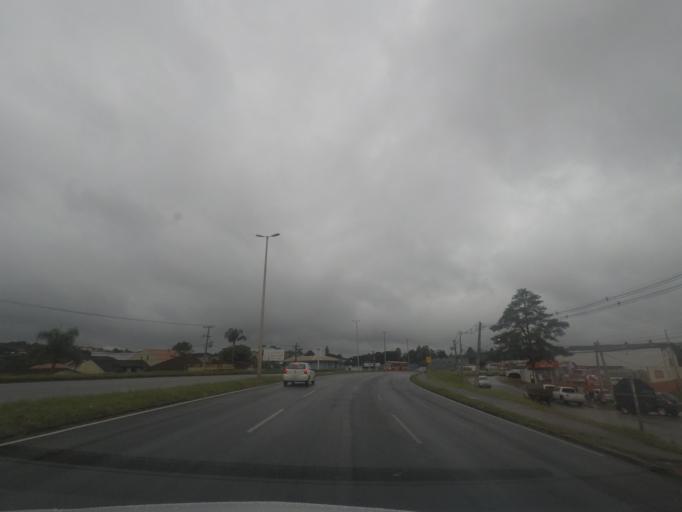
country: BR
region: Parana
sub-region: Colombo
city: Colombo
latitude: -25.3483
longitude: -49.1751
